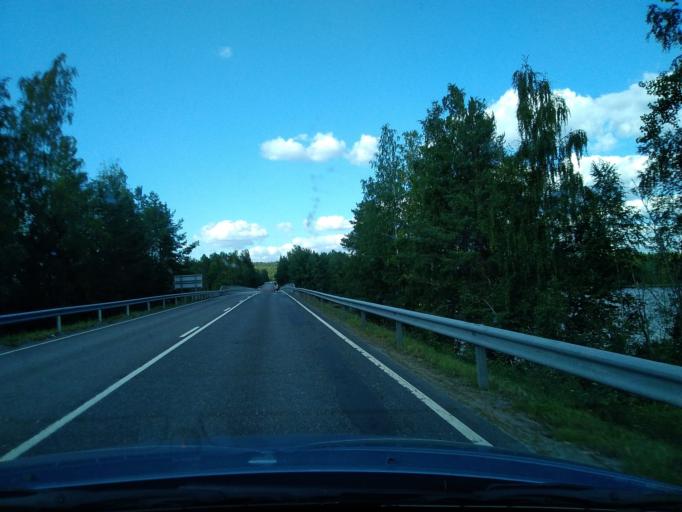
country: FI
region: Pirkanmaa
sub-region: Ylae-Pirkanmaa
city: Maenttae
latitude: 61.9965
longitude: 24.6382
